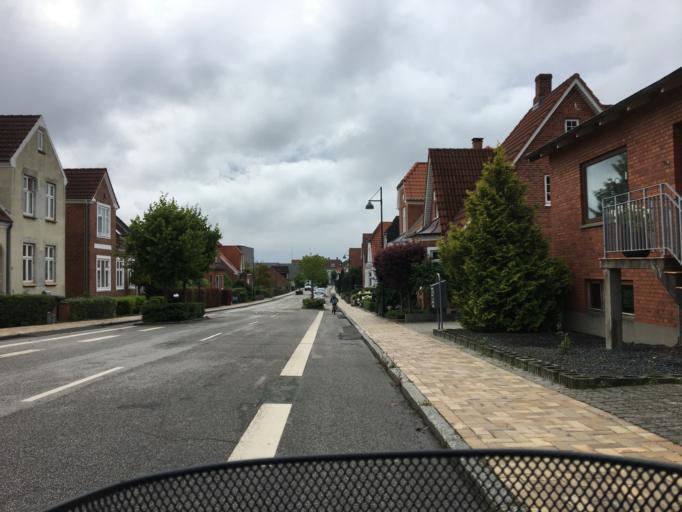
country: DK
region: South Denmark
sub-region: Middelfart Kommune
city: Middelfart
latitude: 55.5036
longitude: 9.7239
